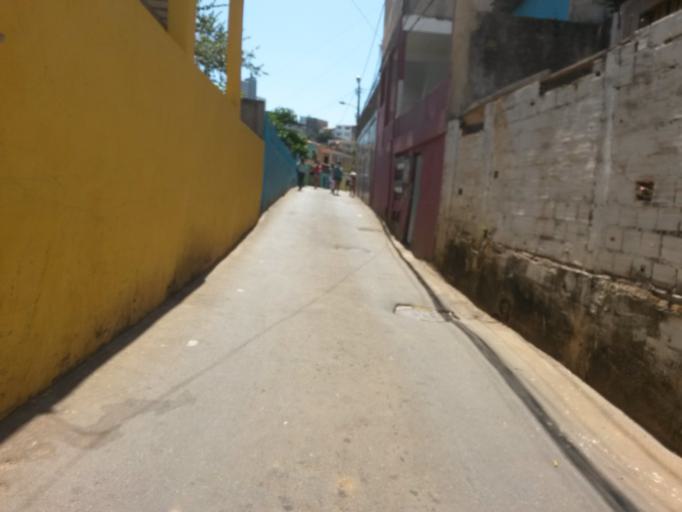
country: BR
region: Bahia
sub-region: Salvador
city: Salvador
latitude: -12.9953
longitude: -38.4804
